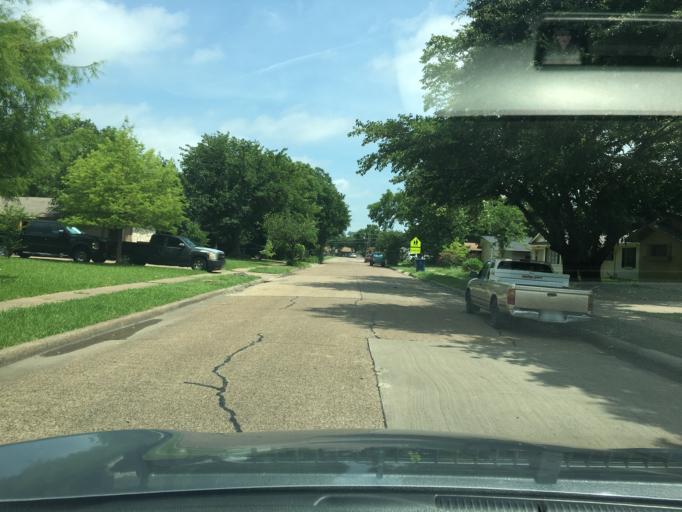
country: US
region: Texas
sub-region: Dallas County
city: Garland
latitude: 32.9219
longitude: -96.6754
